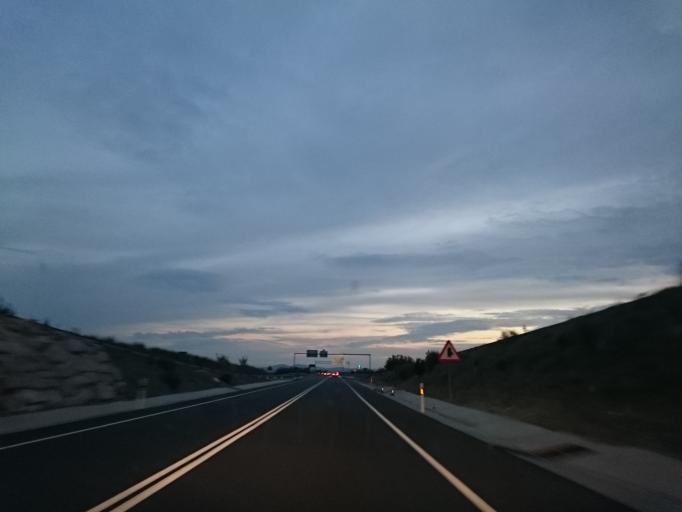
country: ES
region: Catalonia
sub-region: Provincia de Barcelona
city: La Granada
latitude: 41.3754
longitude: 1.7119
